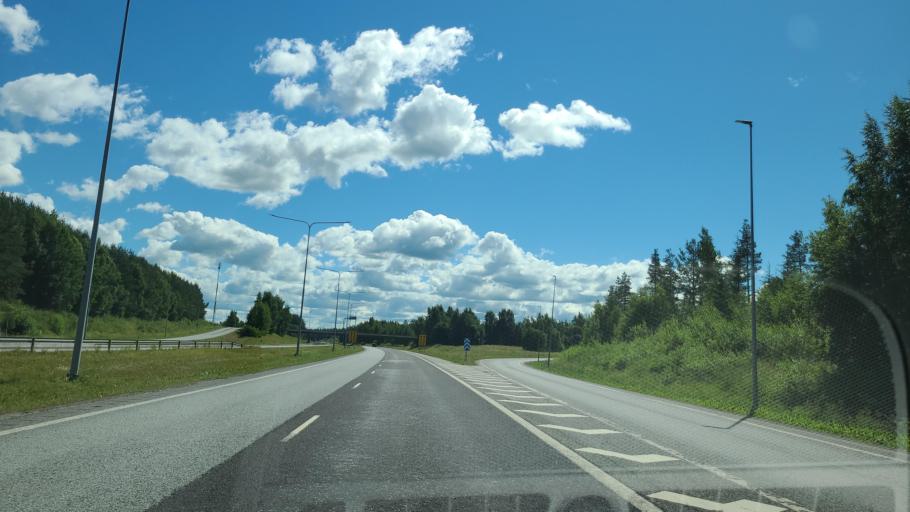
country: FI
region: Ostrobothnia
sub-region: Vaasa
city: Ristinummi
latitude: 63.0308
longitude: 21.7507
